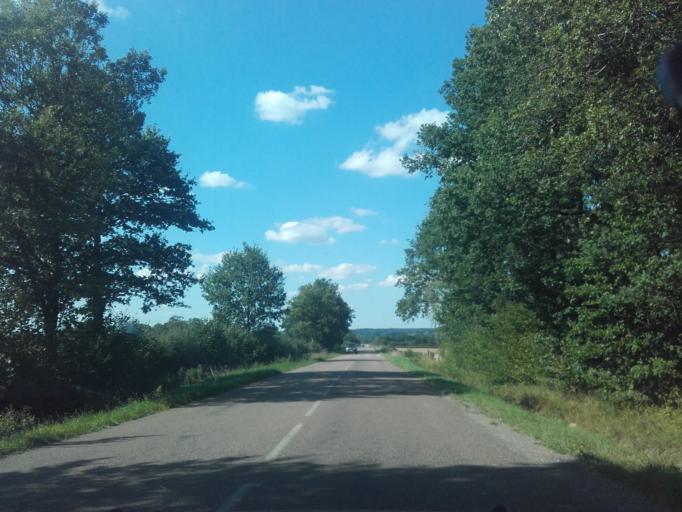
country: FR
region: Bourgogne
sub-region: Departement de Saone-et-Loire
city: Epinac
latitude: 46.9896
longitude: 4.4839
